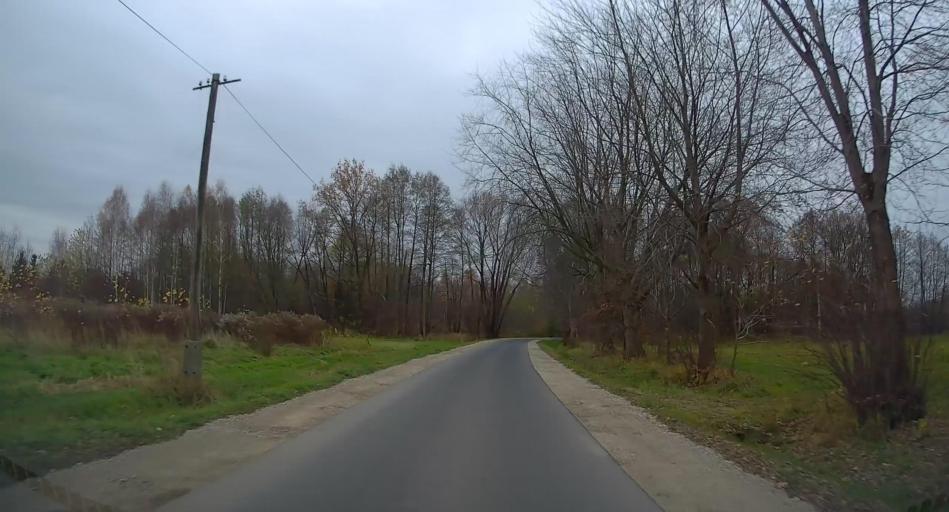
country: PL
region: Lodz Voivodeship
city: Zabia Wola
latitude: 52.0185
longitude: 20.6558
